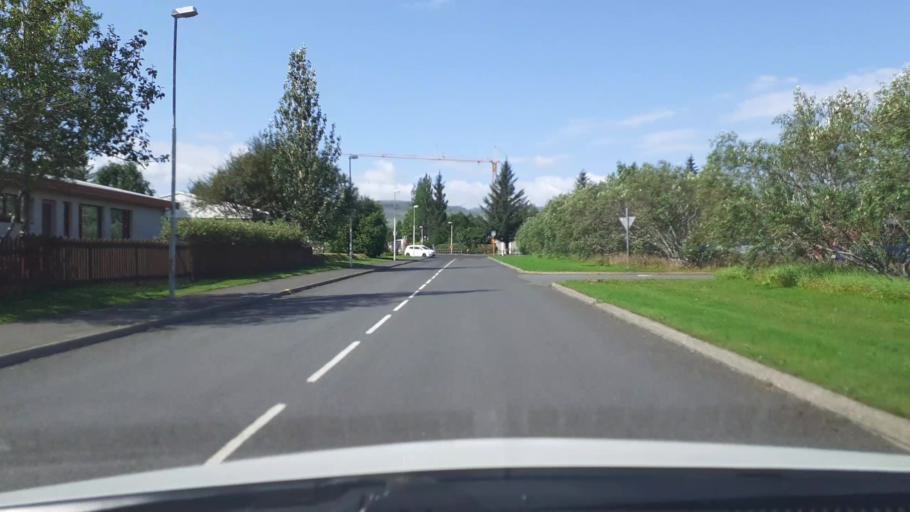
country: IS
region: South
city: Hveragerdi
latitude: 63.9950
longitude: -21.1781
